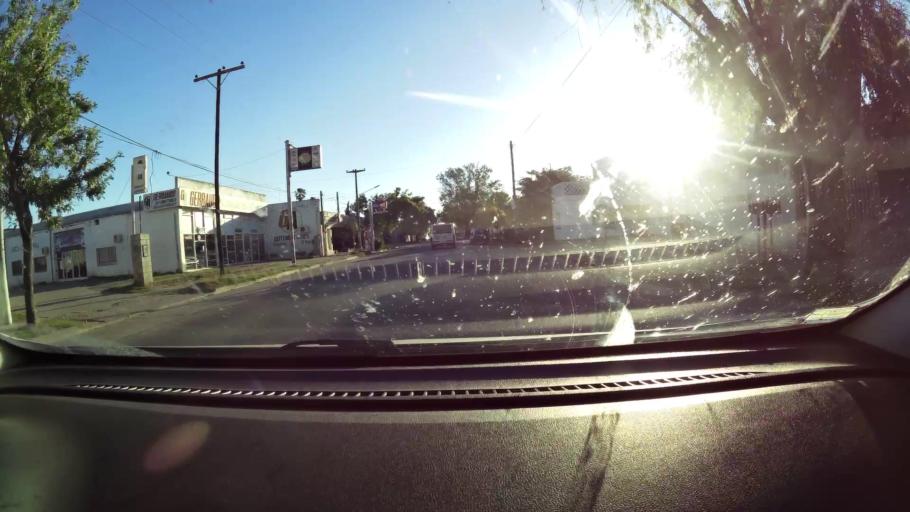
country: AR
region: Cordoba
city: Las Varillas
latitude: -31.8733
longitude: -62.7140
